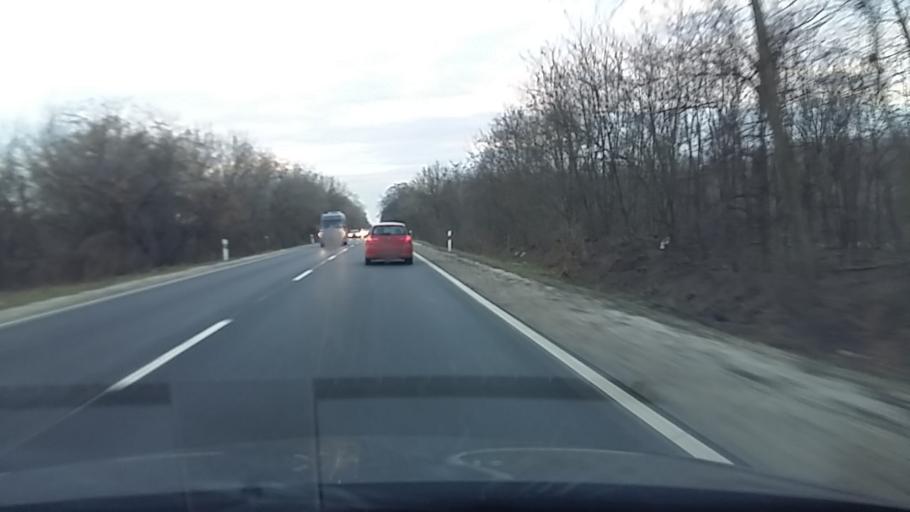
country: HU
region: Hajdu-Bihar
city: Debrecen
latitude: 47.5673
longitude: 21.6523
